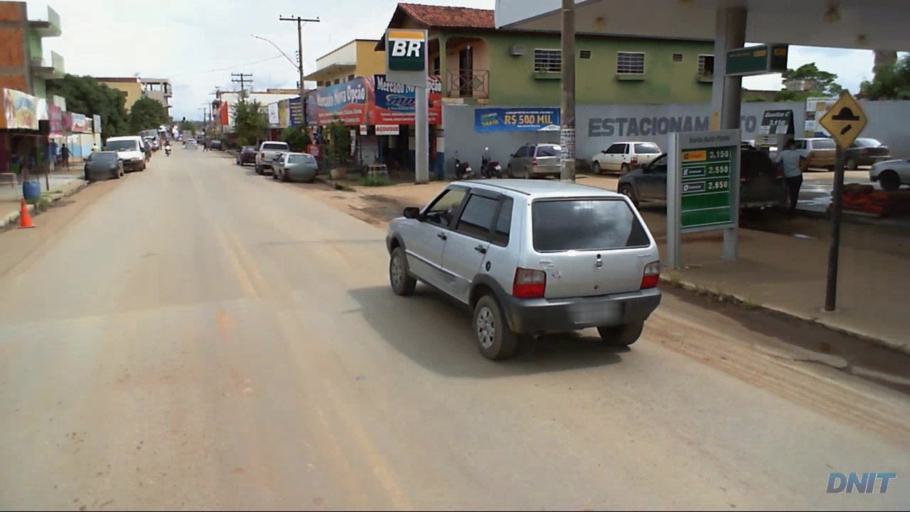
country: BR
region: Goias
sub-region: Padre Bernardo
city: Padre Bernardo
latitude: -15.1697
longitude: -48.2850
